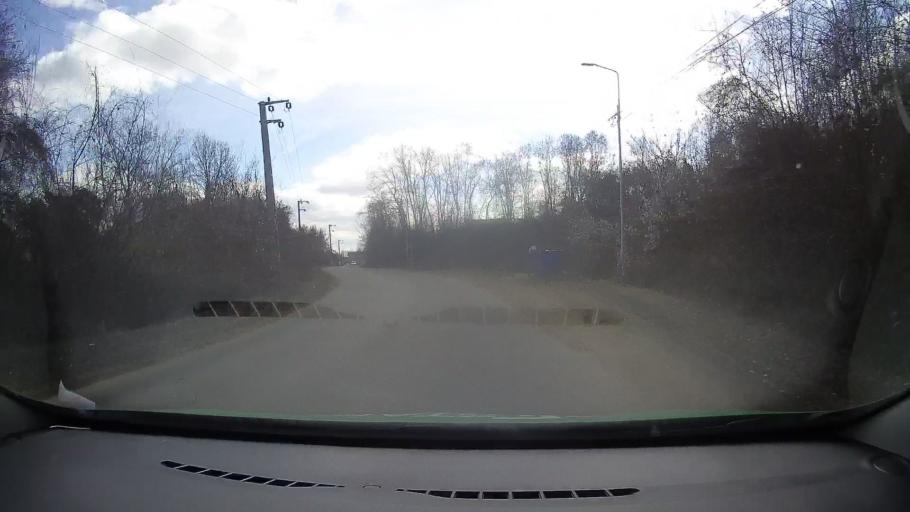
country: RO
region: Dambovita
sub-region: Comuna Sotanga
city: Teis
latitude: 44.9694
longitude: 25.3965
